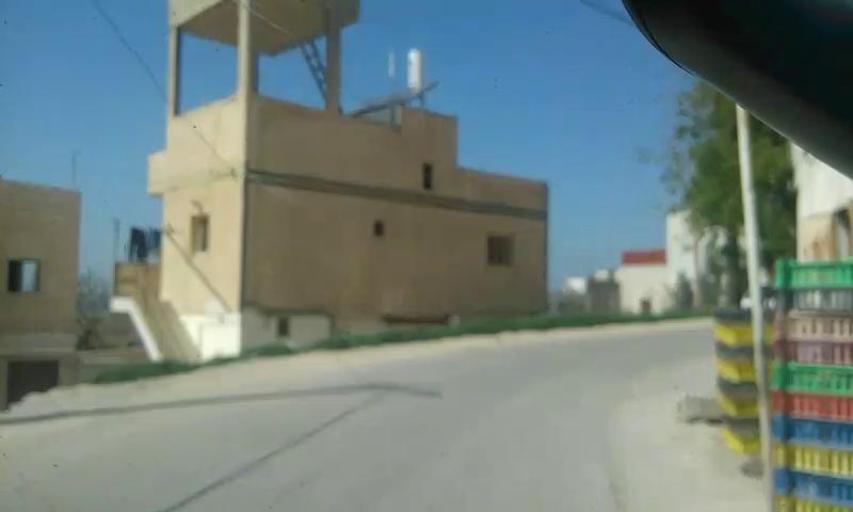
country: PS
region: West Bank
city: Al Majd
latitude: 31.4811
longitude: 34.9497
